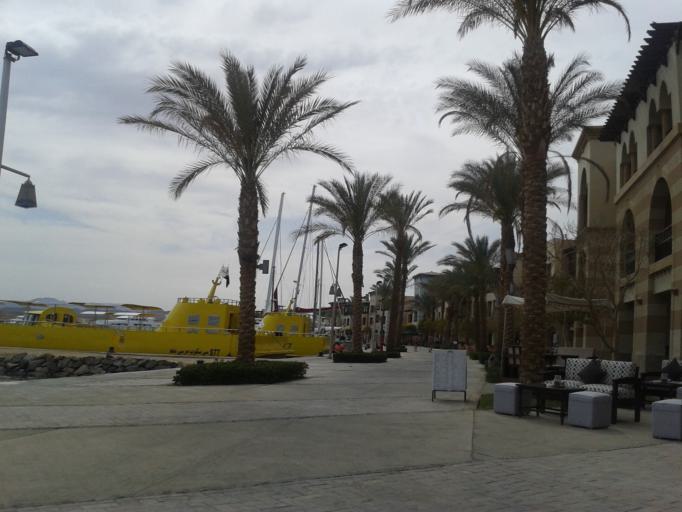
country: EG
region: Red Sea
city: Marsa Alam
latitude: 25.5342
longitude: 34.6372
